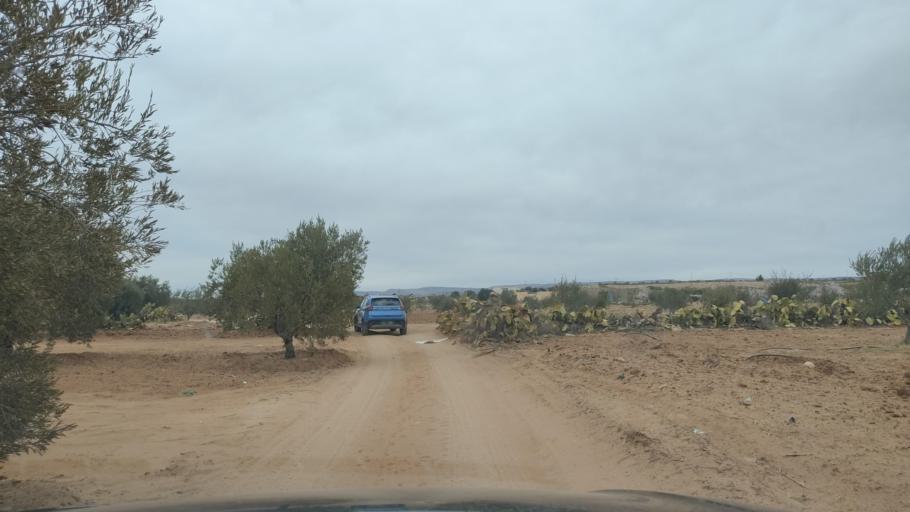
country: TN
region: Al Qasrayn
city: Kasserine
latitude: 35.2272
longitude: 8.9176
